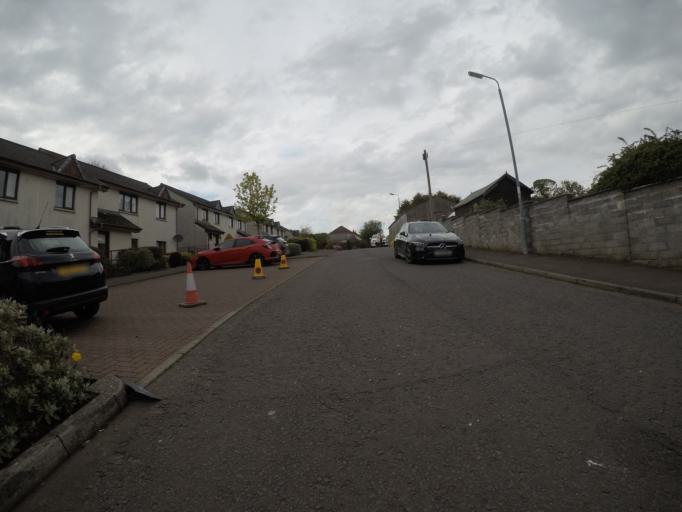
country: GB
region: Scotland
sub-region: East Ayrshire
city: Kilmaurs
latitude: 55.6389
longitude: -4.5297
